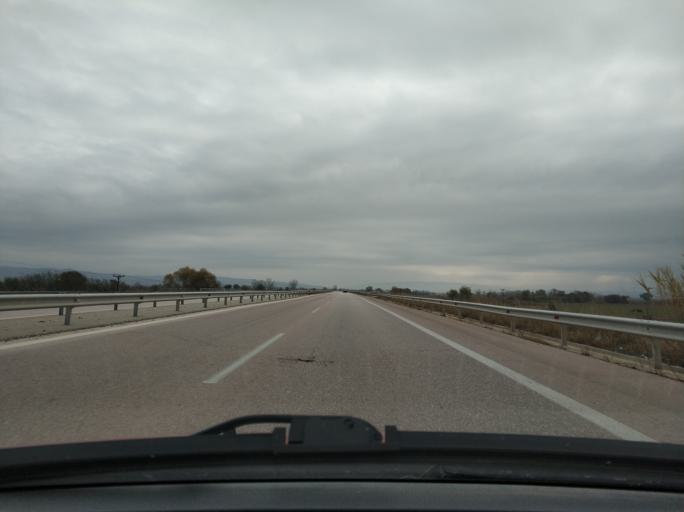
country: GR
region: Central Macedonia
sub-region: Nomos Thessalonikis
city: Lagkadas
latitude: 40.7284
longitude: 23.0660
